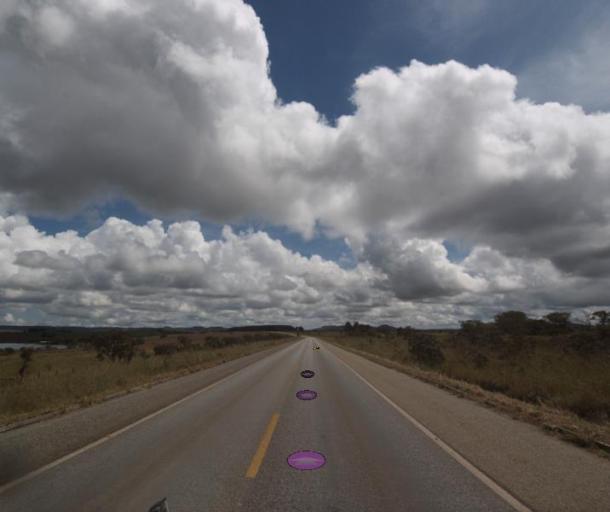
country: BR
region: Goias
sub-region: Pirenopolis
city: Pirenopolis
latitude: -15.7489
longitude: -48.6610
